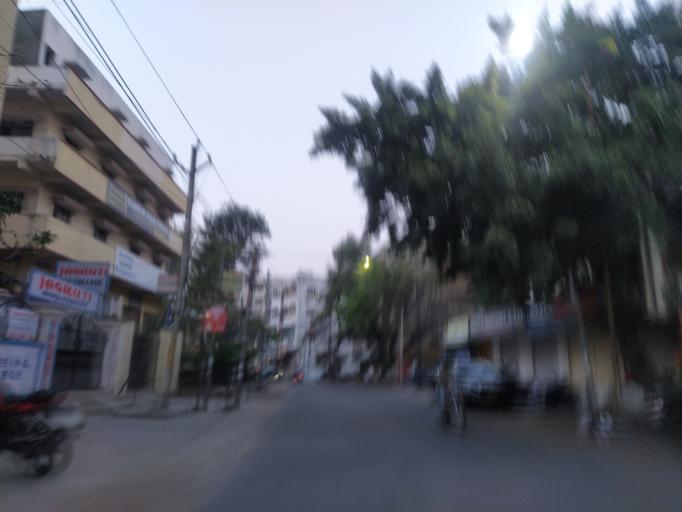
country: IN
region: Telangana
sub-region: Hyderabad
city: Hyderabad
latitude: 17.3932
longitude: 78.4868
